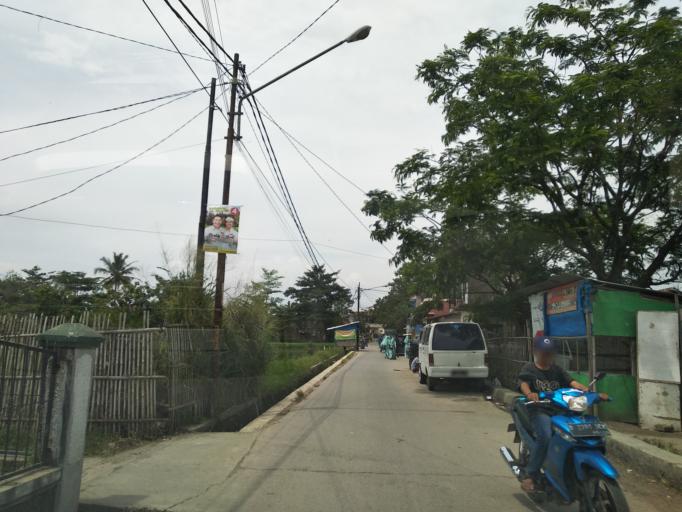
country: ID
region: West Java
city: Pameungpeuk
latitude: -6.9760
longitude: 107.6478
